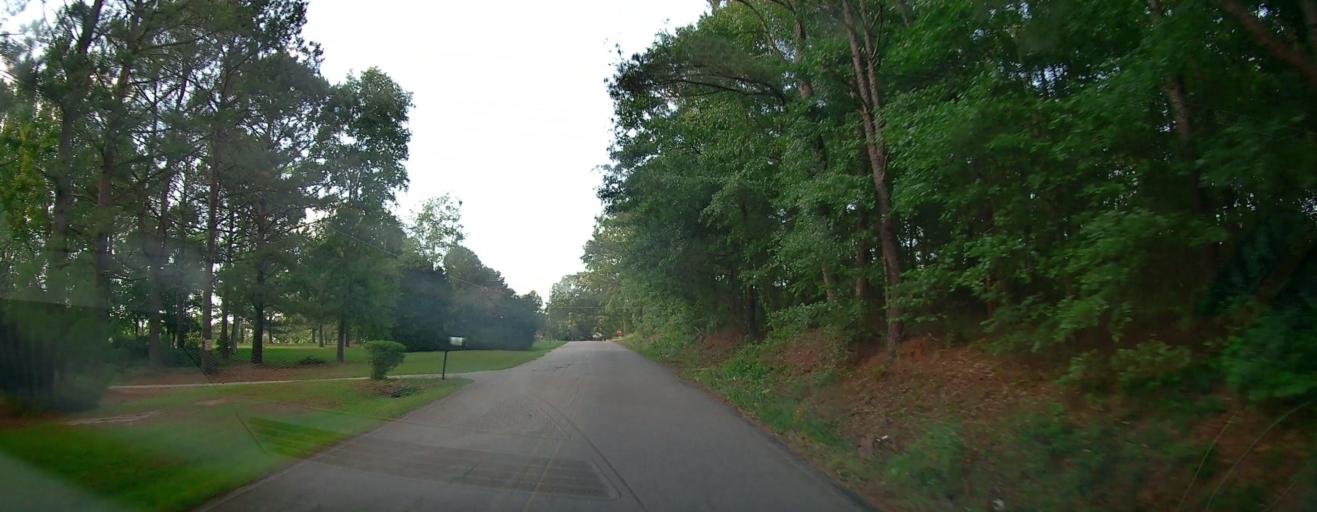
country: US
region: Georgia
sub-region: Peach County
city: Byron
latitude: 32.6174
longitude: -83.7736
